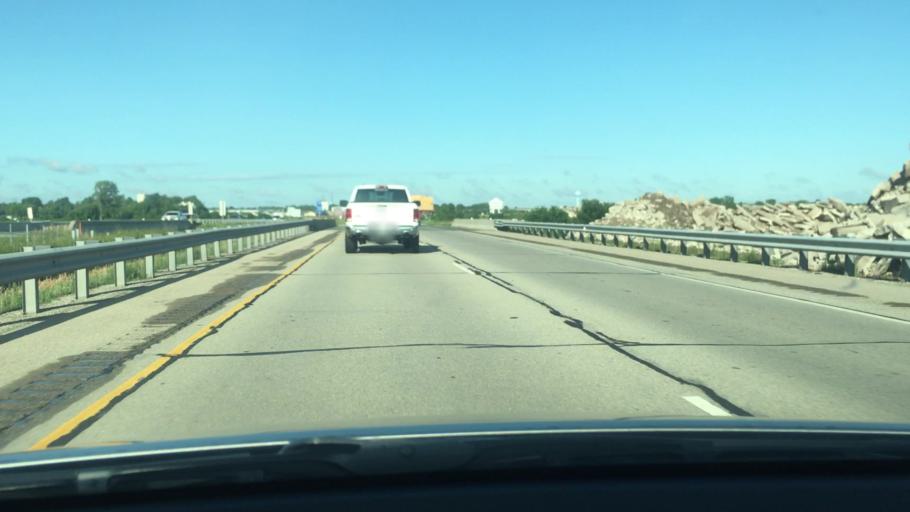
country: US
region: Wisconsin
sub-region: Outagamie County
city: Kaukauna
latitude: 44.2998
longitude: -88.2720
